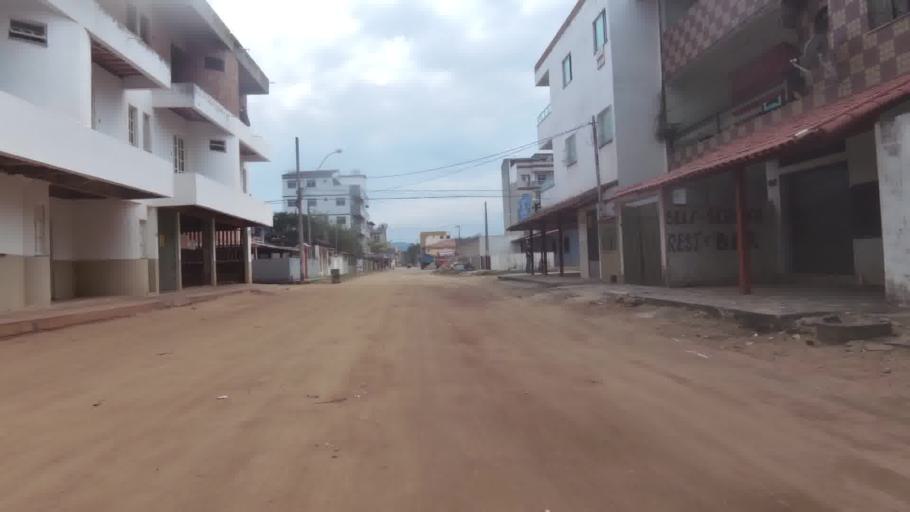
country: BR
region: Espirito Santo
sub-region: Piuma
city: Piuma
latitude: -20.8480
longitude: -40.7458
